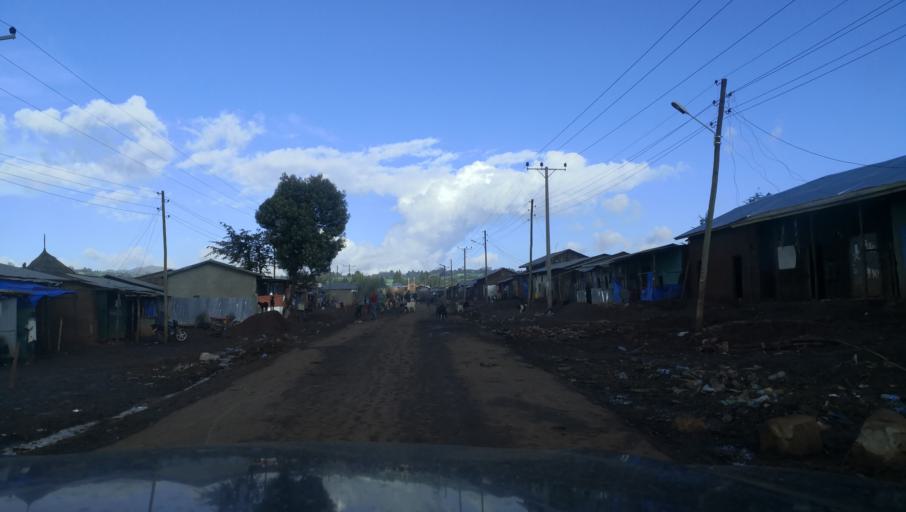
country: ET
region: Oromiya
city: Tulu Bolo
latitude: 8.3935
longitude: 38.2864
